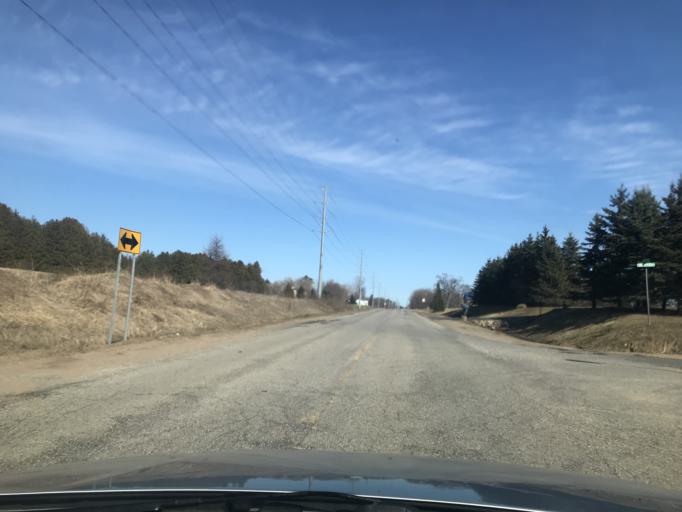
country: US
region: Michigan
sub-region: Menominee County
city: Menominee
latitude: 45.1447
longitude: -87.6384
